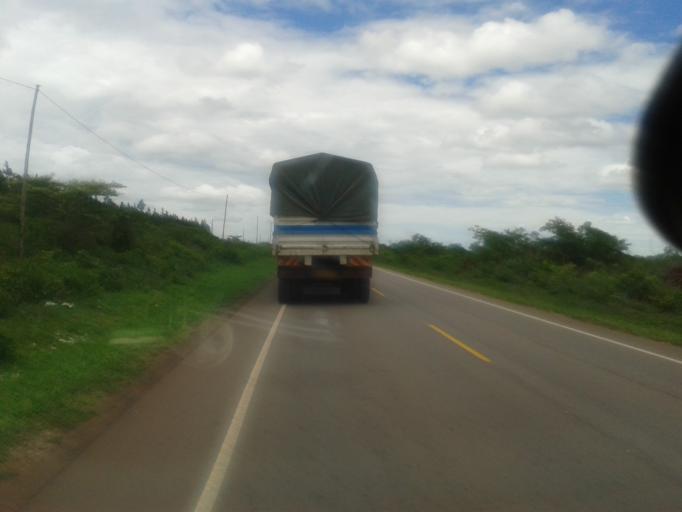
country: UG
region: Western Region
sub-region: Kiryandongo District
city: Masindi Port
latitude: 1.7479
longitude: 32.0226
